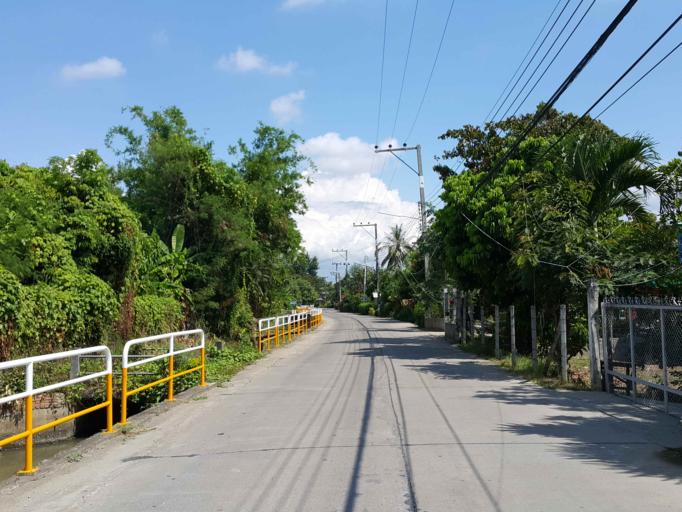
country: TH
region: Chiang Mai
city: Saraphi
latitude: 18.7276
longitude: 99.0449
